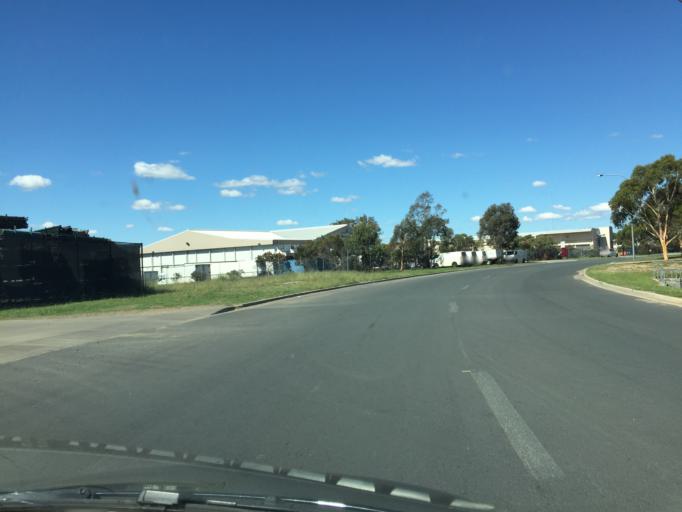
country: AU
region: Australian Capital Territory
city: Macarthur
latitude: -35.3953
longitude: 149.1585
